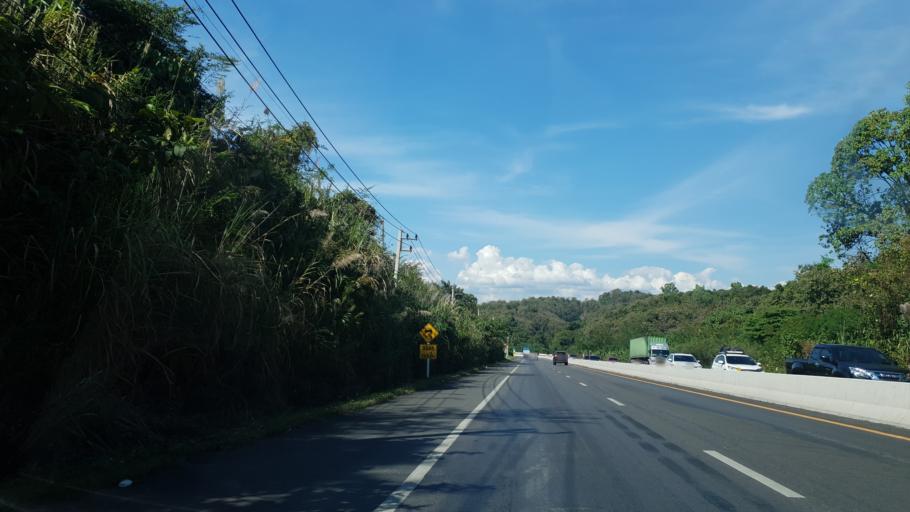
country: TH
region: Phrae
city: Den Chai
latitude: 17.8425
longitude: 100.0522
